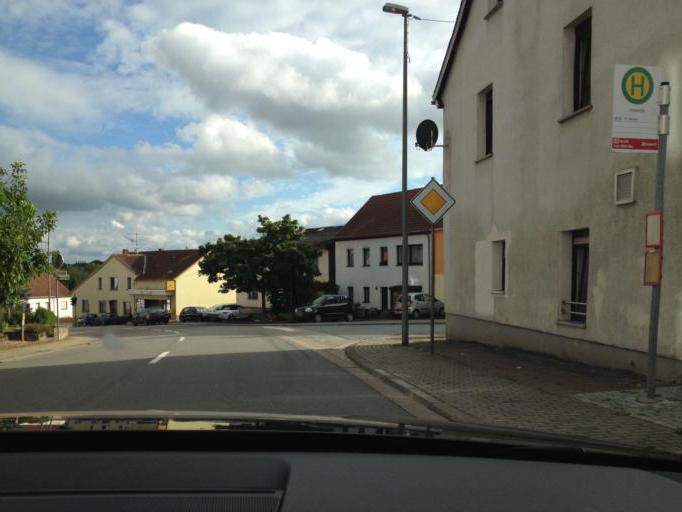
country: DE
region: Saarland
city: Sankt Wendel
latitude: 49.4952
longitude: 7.1638
